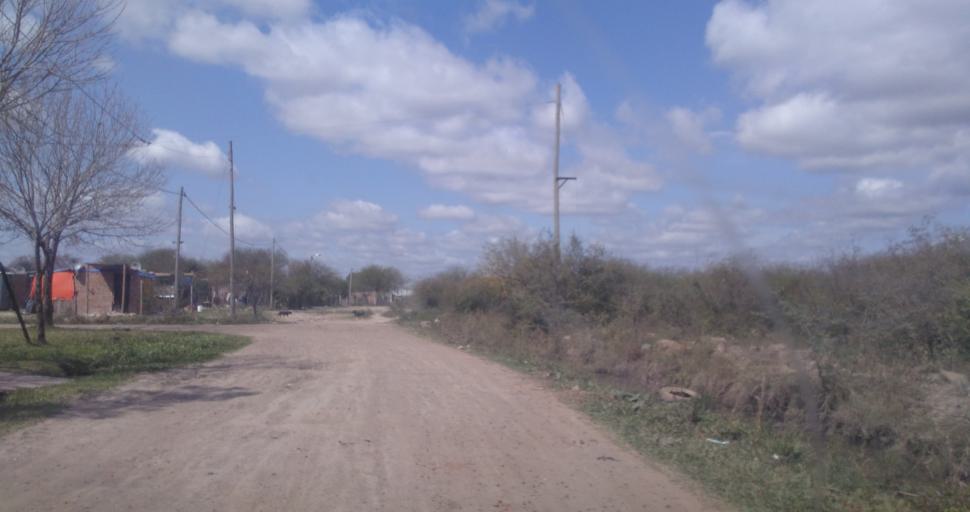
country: AR
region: Chaco
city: Fontana
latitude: -27.4324
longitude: -59.0336
